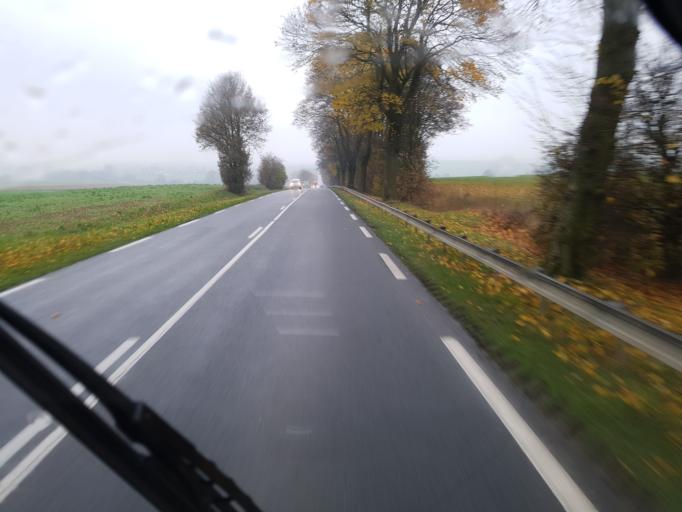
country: FR
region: Picardie
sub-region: Departement de l'Aisne
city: Omissy
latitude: 49.9086
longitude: 3.2584
